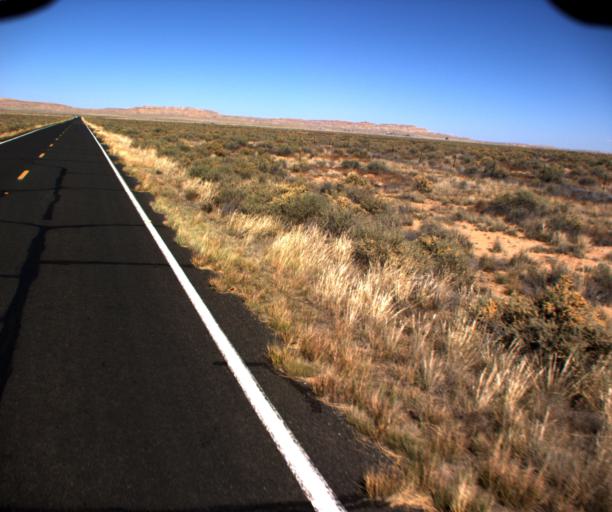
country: US
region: Arizona
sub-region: Navajo County
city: First Mesa
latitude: 35.7182
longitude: -110.5140
